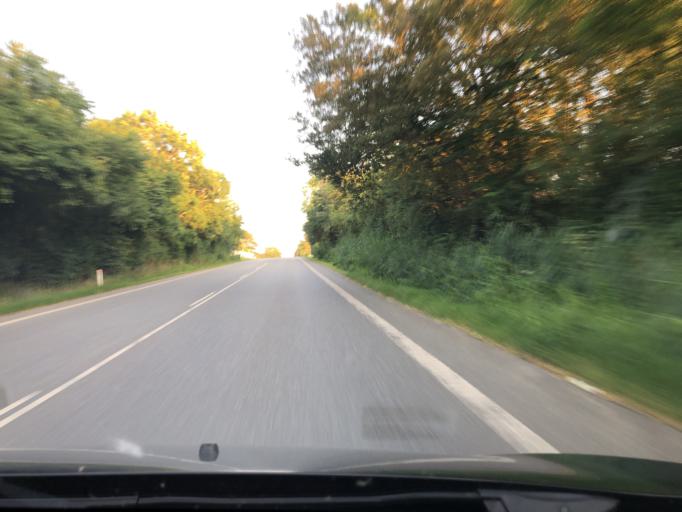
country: DK
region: South Denmark
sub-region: Fredericia Kommune
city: Snoghoj
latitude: 55.5525
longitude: 9.6770
